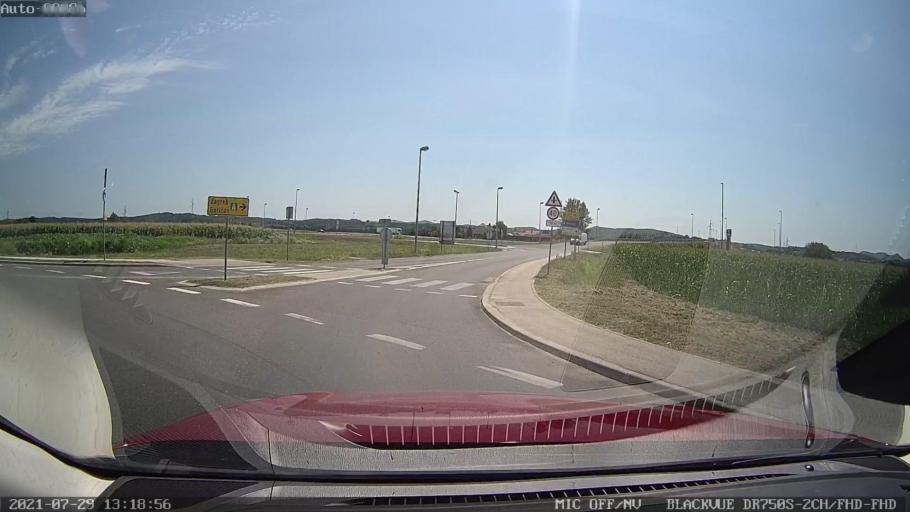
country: HR
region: Varazdinska
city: Varazdin
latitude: 46.2669
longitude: 16.3814
